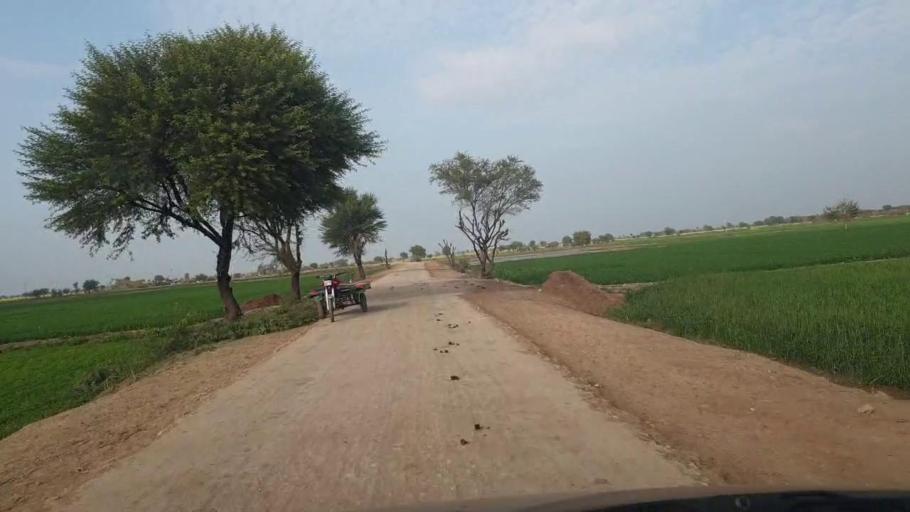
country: PK
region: Sindh
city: Shahdadpur
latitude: 25.8882
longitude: 68.7260
